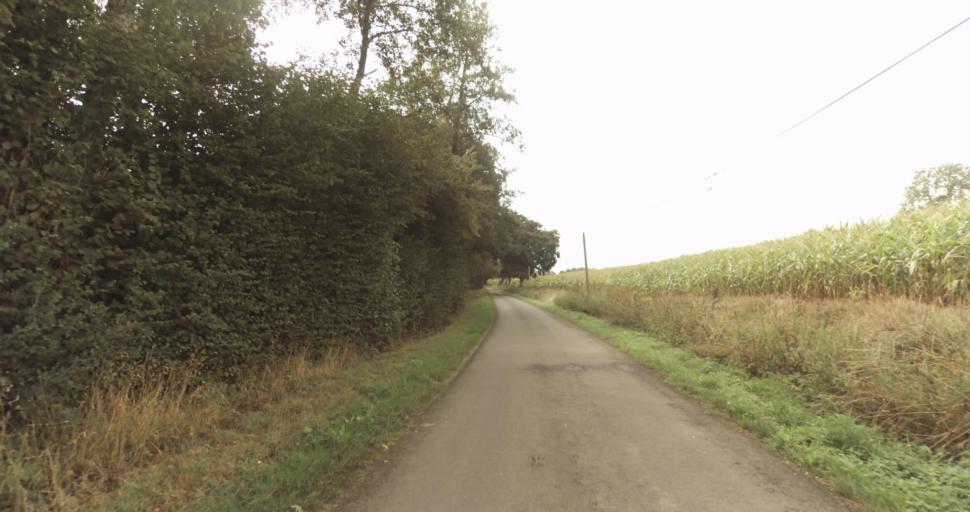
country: FR
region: Lower Normandy
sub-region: Departement de l'Orne
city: Gace
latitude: 48.8248
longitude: 0.3689
